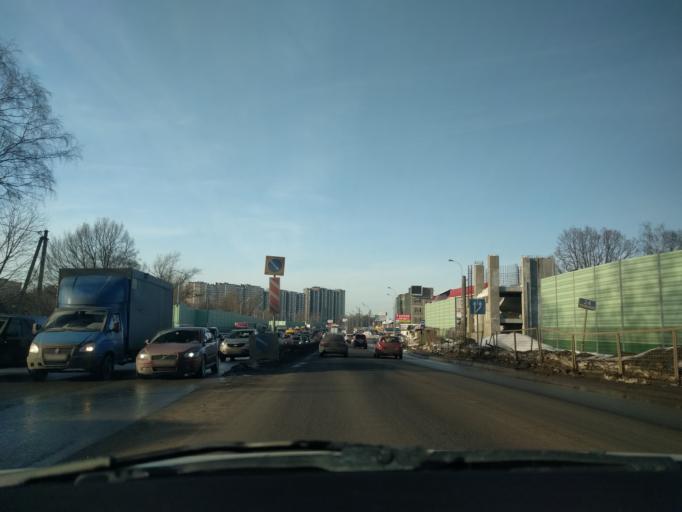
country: RU
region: Moscow
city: Severnyy
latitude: 55.9557
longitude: 37.5355
